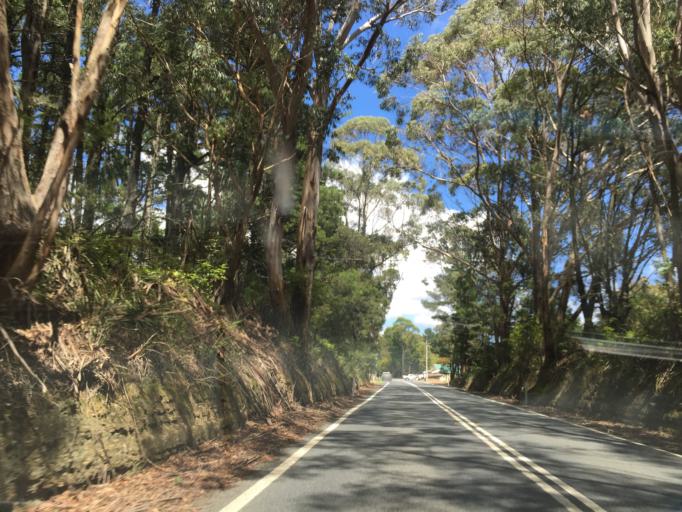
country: AU
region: New South Wales
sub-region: Blue Mountains Municipality
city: Lawson
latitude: -33.5206
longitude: 150.4630
